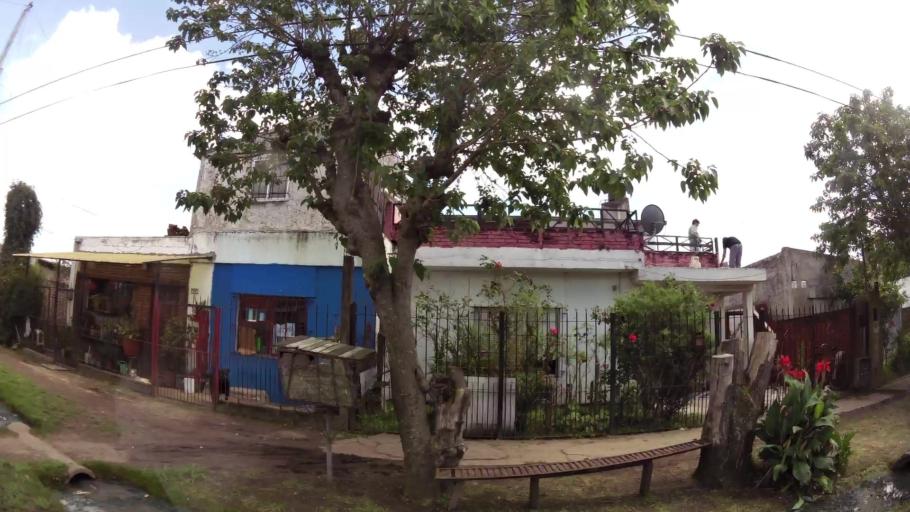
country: AR
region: Buenos Aires
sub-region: Partido de Quilmes
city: Quilmes
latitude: -34.8326
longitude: -58.2275
